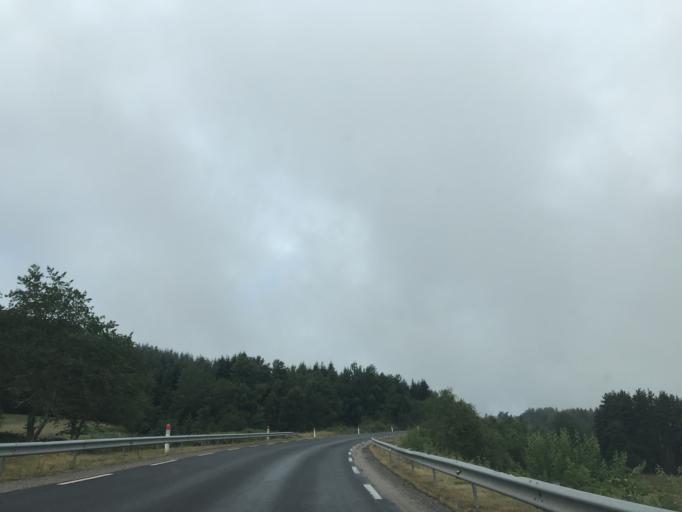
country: FR
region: Auvergne
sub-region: Departement de la Haute-Loire
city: Fontannes
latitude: 45.3491
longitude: 3.7344
